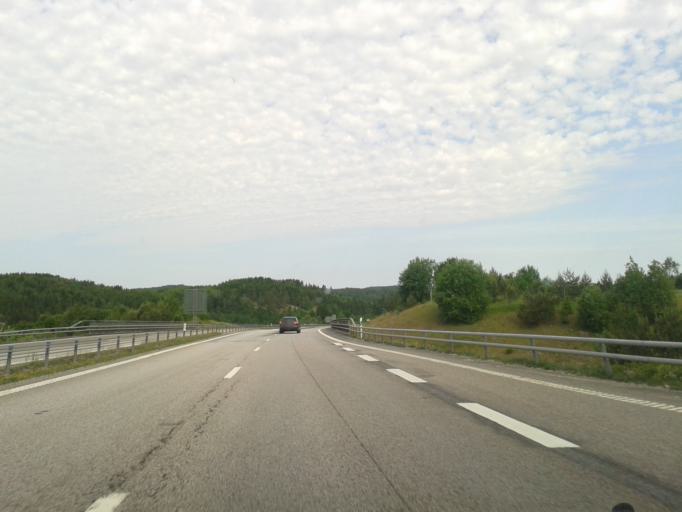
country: SE
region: Vaestra Goetaland
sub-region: Munkedals Kommun
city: Munkedal
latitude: 58.4889
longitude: 11.5823
